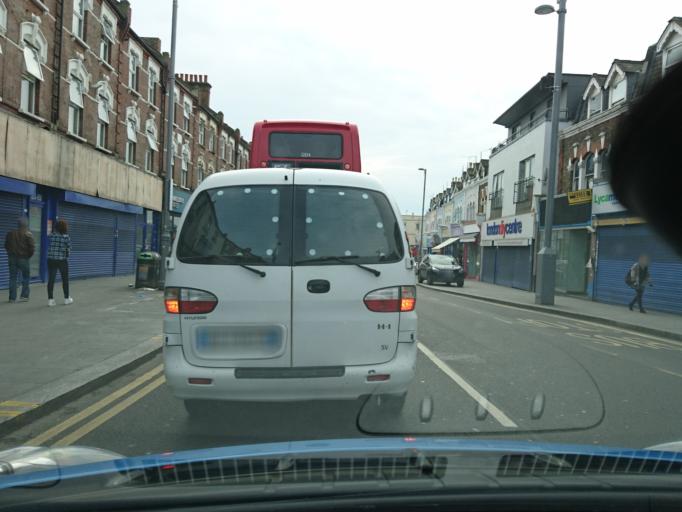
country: GB
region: England
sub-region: Greater London
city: Walthamstow
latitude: 51.5763
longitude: -0.0116
